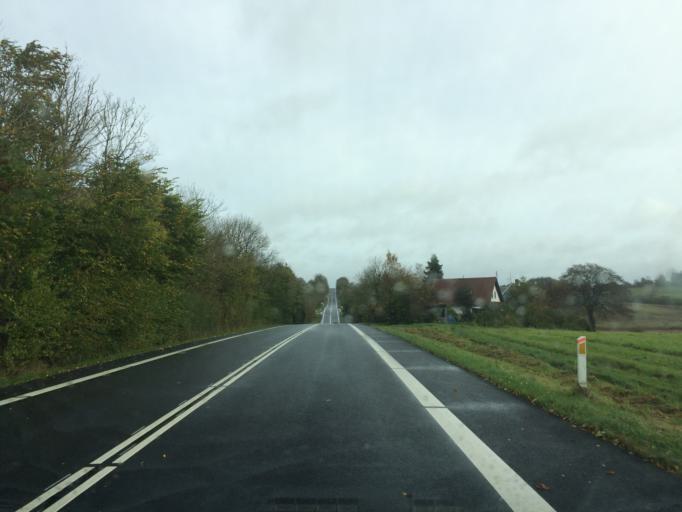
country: DK
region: South Denmark
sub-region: Fredericia Kommune
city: Taulov
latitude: 55.5311
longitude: 9.5821
